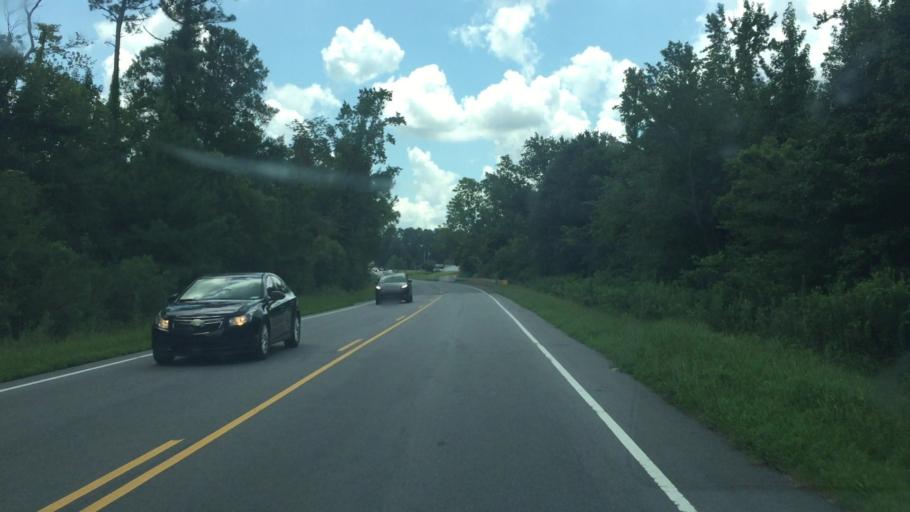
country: US
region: North Carolina
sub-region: Columbus County
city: Chadbourn
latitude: 34.2566
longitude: -78.8179
